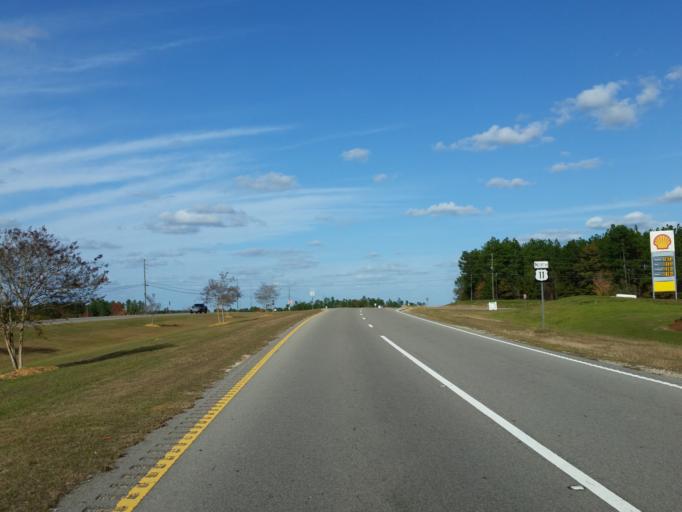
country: US
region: Mississippi
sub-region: Lamar County
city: West Hattiesburg
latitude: 31.2630
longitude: -89.3363
